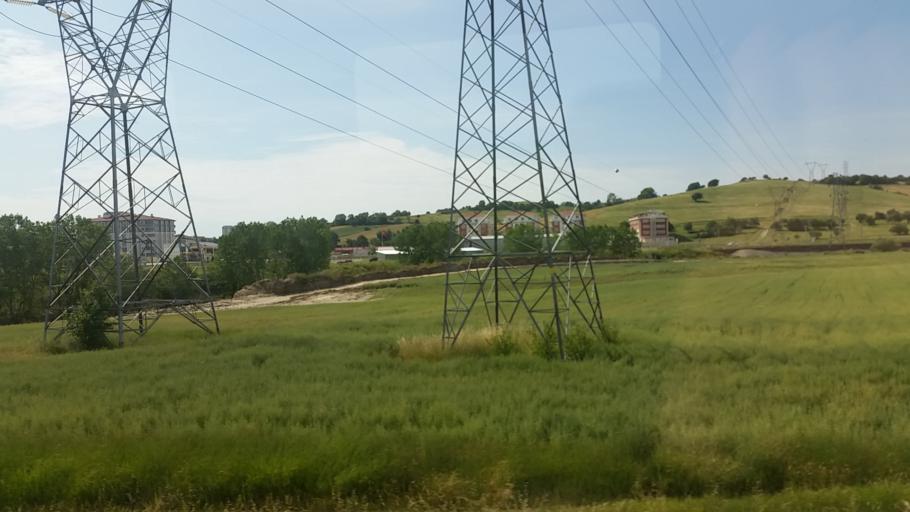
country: TR
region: Tekirdag
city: Cerkezkoey
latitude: 41.2687
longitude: 27.9531
